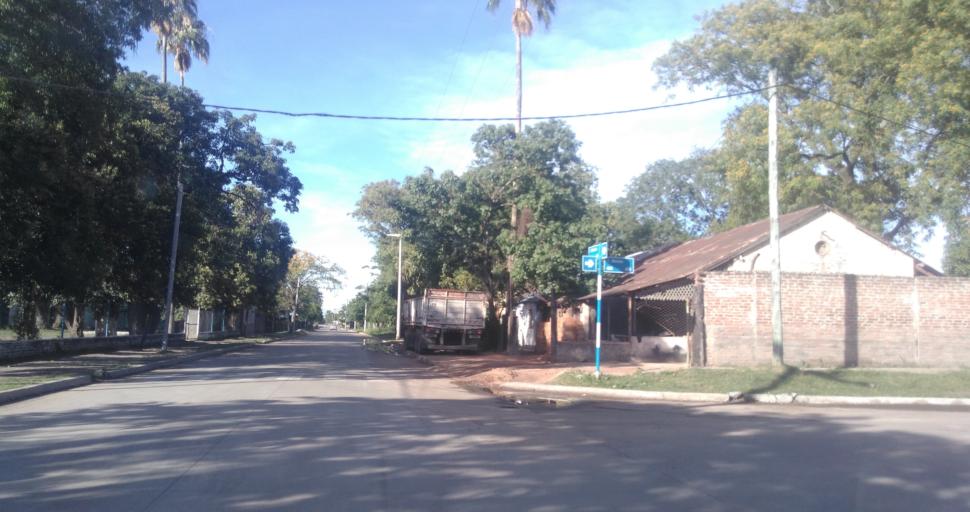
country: AR
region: Chaco
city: Fontana
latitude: -27.4182
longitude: -59.0322
